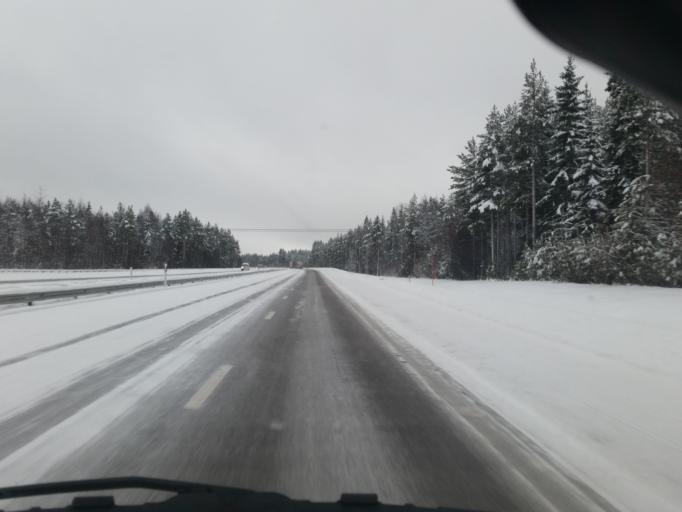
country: SE
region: Norrbotten
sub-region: Pitea Kommun
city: Pitea
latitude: 65.3490
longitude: 21.4378
